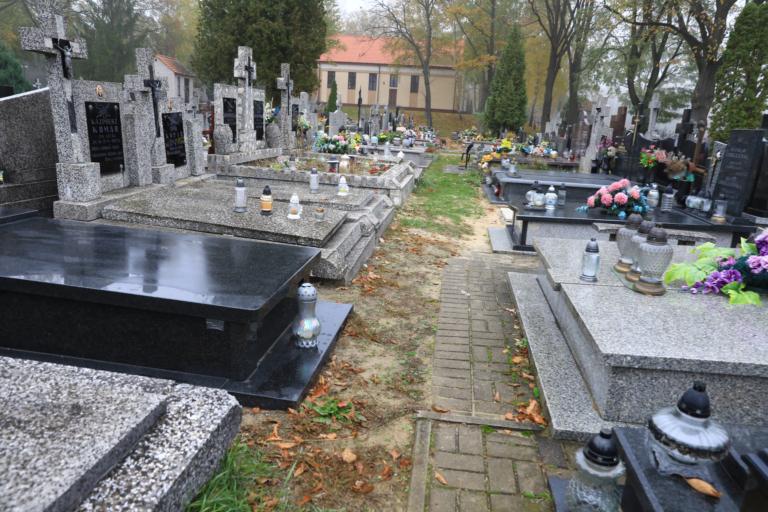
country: PL
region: Masovian Voivodeship
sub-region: Powiat wolominski
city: Nowe Lipiny
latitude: 52.3306
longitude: 21.2715
